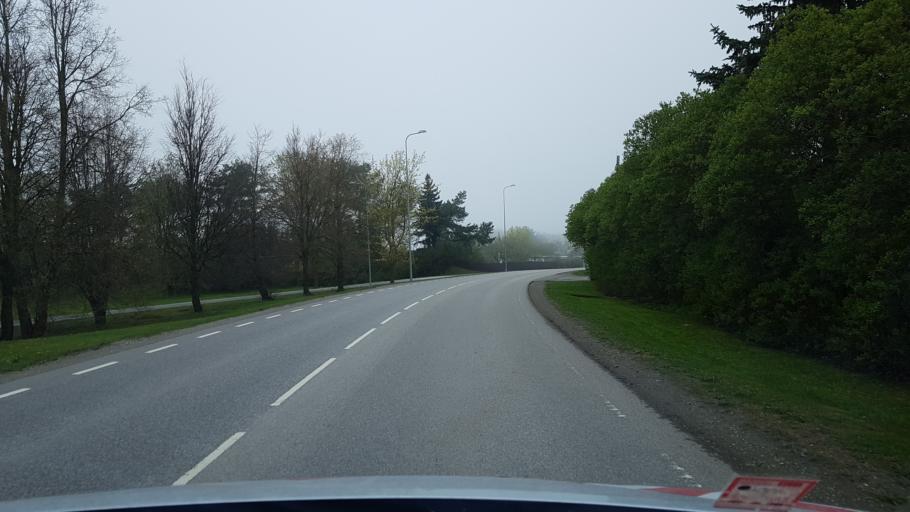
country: EE
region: Harju
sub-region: Joelaehtme vald
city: Loo
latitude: 59.4335
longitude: 24.9387
